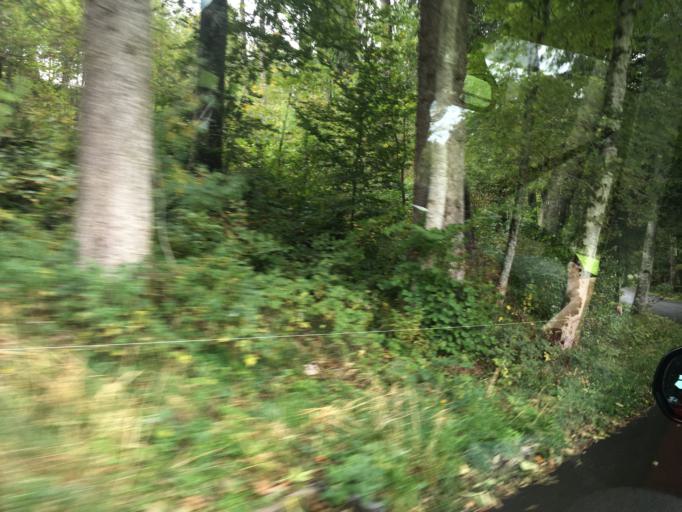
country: CH
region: Bern
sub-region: Bern-Mittelland District
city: Guggisberg
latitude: 46.7627
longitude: 7.3509
